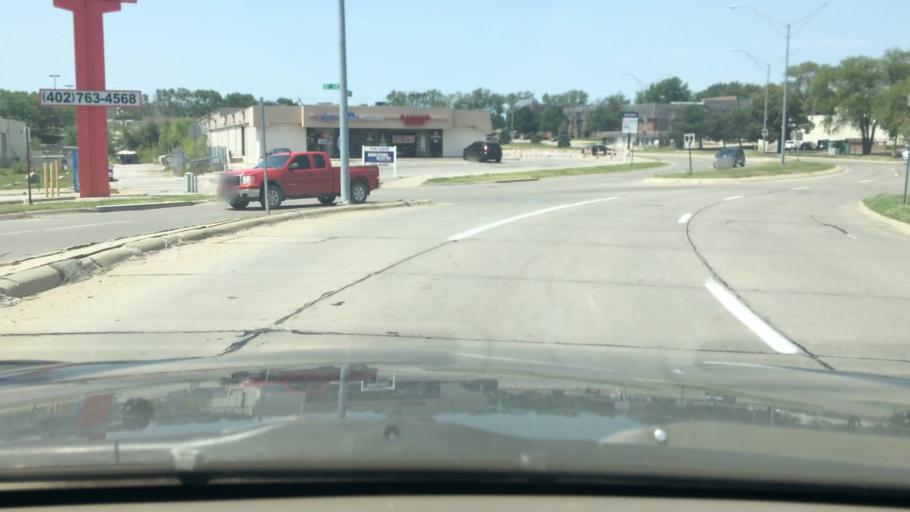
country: US
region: Nebraska
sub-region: Douglas County
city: Ralston
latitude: 41.2008
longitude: -96.0437
